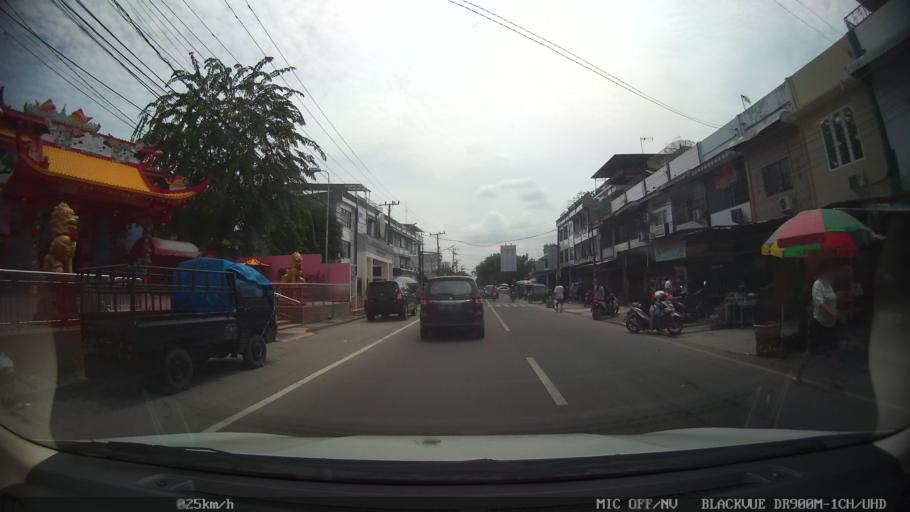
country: ID
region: North Sumatra
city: Sunggal
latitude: 3.5749
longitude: 98.6119
